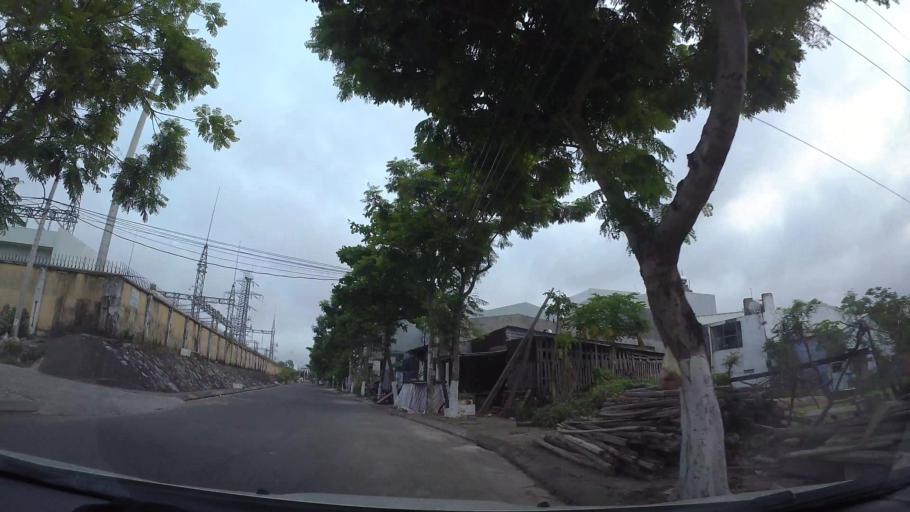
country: VN
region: Da Nang
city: Son Tra
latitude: 16.0400
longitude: 108.2402
